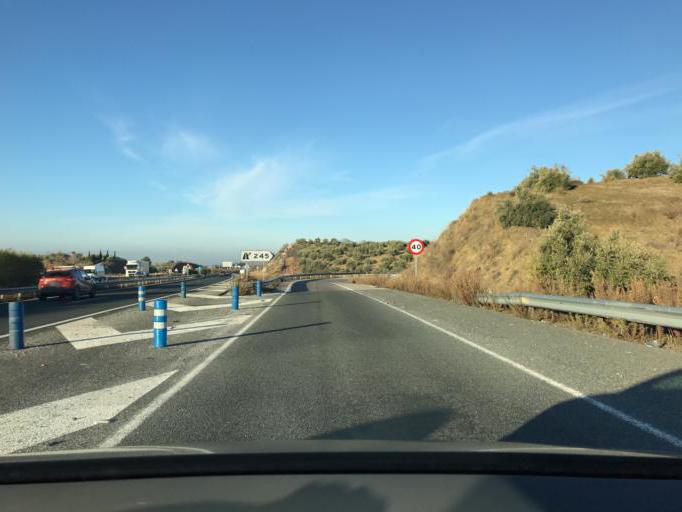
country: ES
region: Andalusia
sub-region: Provincia de Granada
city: Pulianas
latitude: 37.2394
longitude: -3.6086
